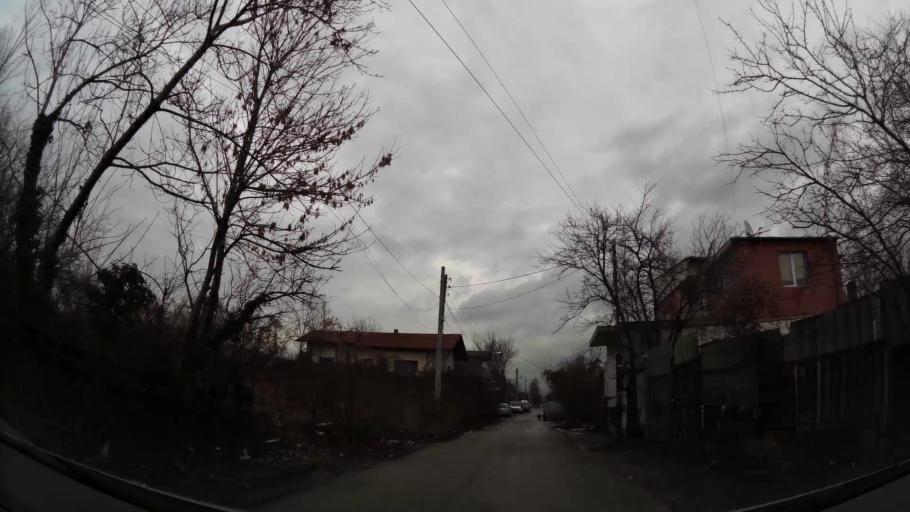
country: BG
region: Sofia-Capital
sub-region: Stolichna Obshtina
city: Sofia
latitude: 42.7222
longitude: 23.2797
